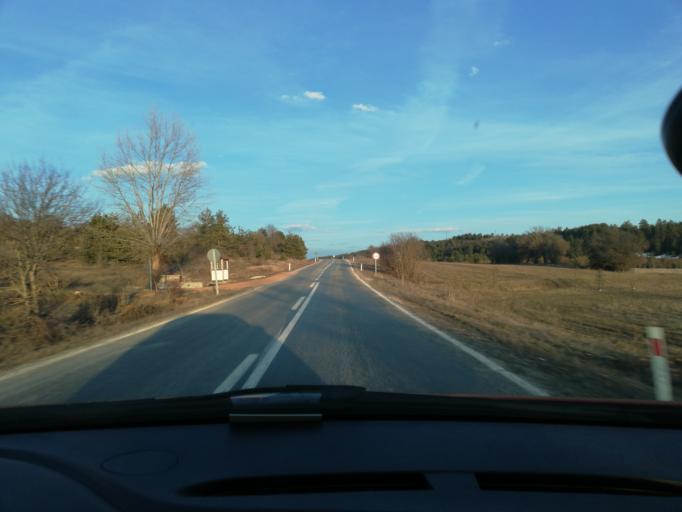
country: TR
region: Kastamonu
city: Agli
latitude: 41.6952
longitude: 33.6175
